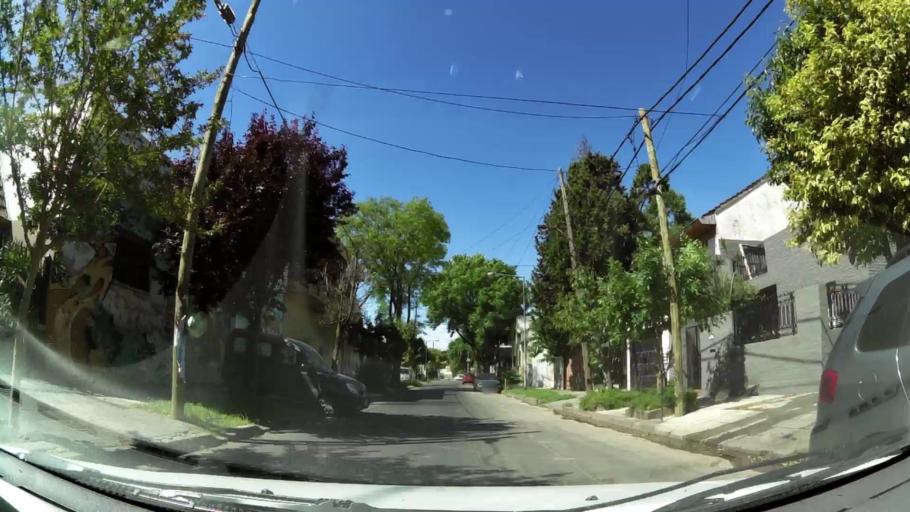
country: AR
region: Buenos Aires
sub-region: Partido de General San Martin
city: General San Martin
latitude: -34.5492
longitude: -58.5640
